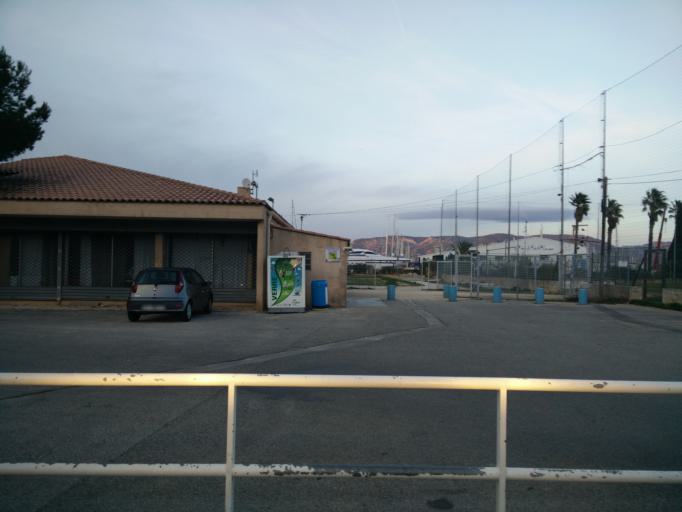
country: FR
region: Provence-Alpes-Cote d'Azur
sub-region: Departement du Var
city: Saint-Mandrier-sur-Mer
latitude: 43.0774
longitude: 5.9055
